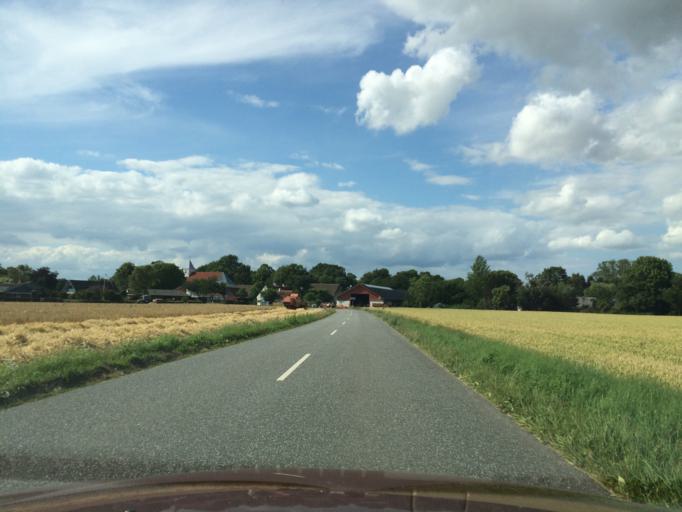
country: DK
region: Central Jutland
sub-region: Syddjurs Kommune
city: Ebeltoft
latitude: 56.3007
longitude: 10.6961
